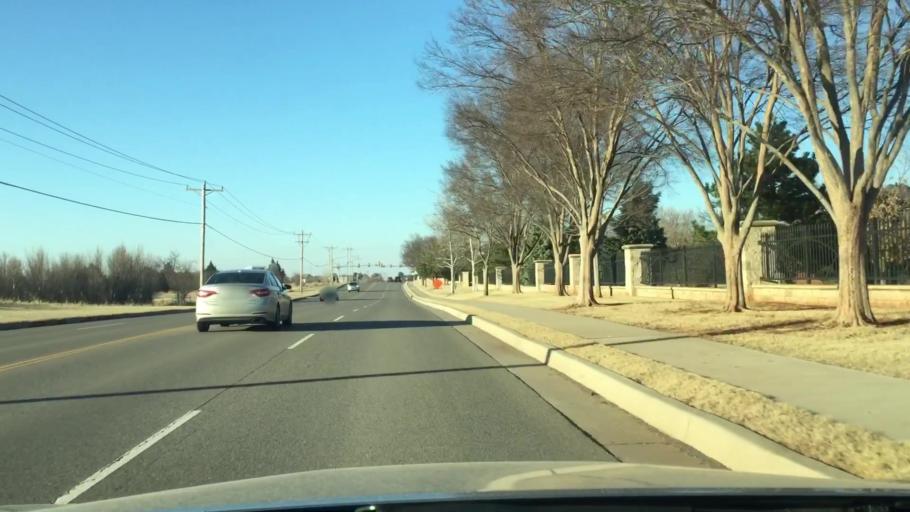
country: US
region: Oklahoma
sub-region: Oklahoma County
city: The Village
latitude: 35.6205
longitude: -97.6207
